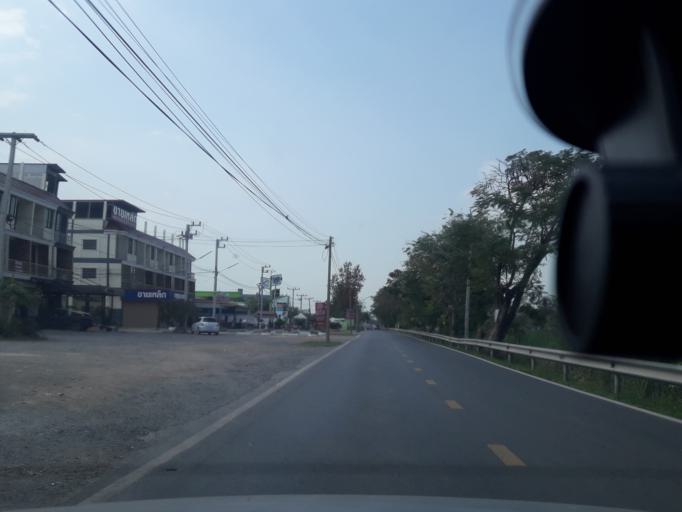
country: TH
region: Sara Buri
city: Nong Khae
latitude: 14.3367
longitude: 100.8643
